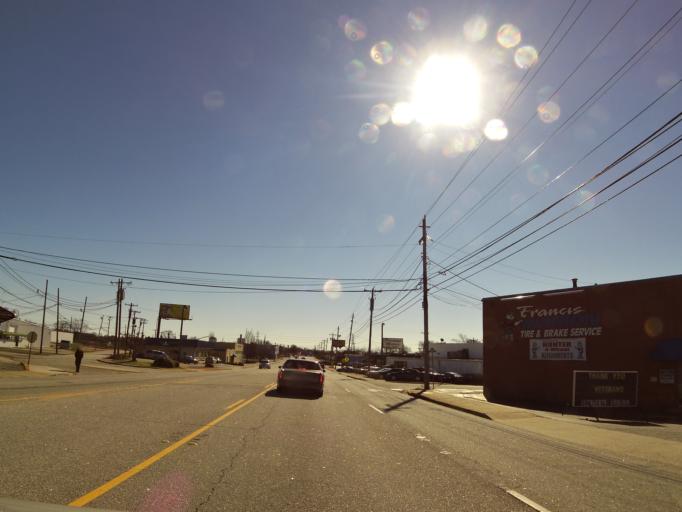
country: US
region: South Carolina
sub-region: Greenville County
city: Sans Souci
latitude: 34.8826
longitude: -82.4050
